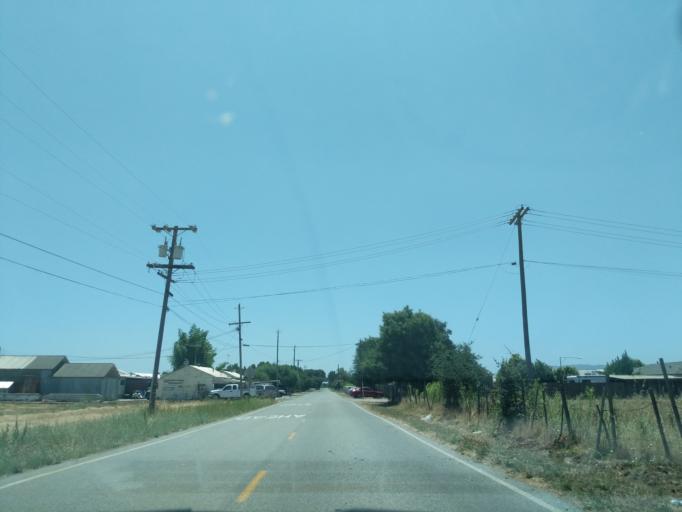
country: US
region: California
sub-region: Santa Clara County
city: San Martin
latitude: 37.1016
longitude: -121.6156
